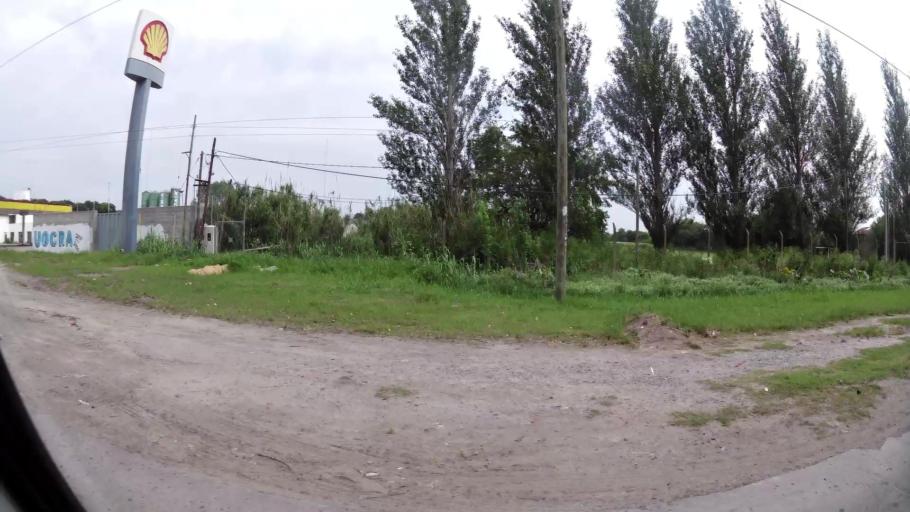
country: AR
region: Buenos Aires
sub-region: Partido de La Plata
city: La Plata
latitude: -34.9120
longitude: -58.0064
